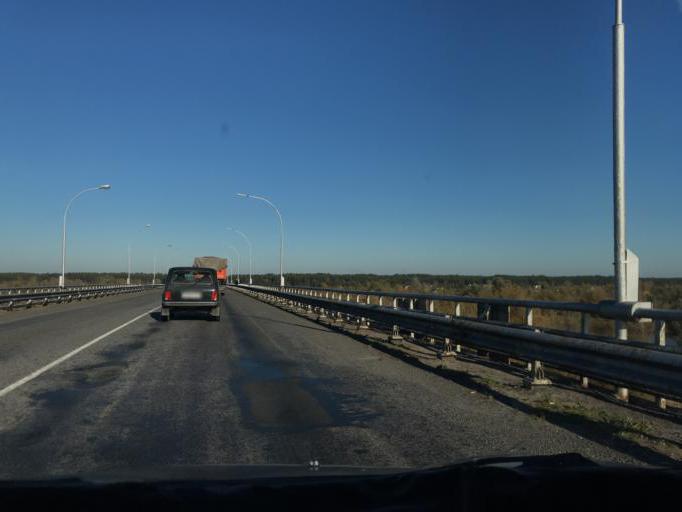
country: BY
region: Gomel
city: Mazyr
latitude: 52.0252
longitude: 29.3216
